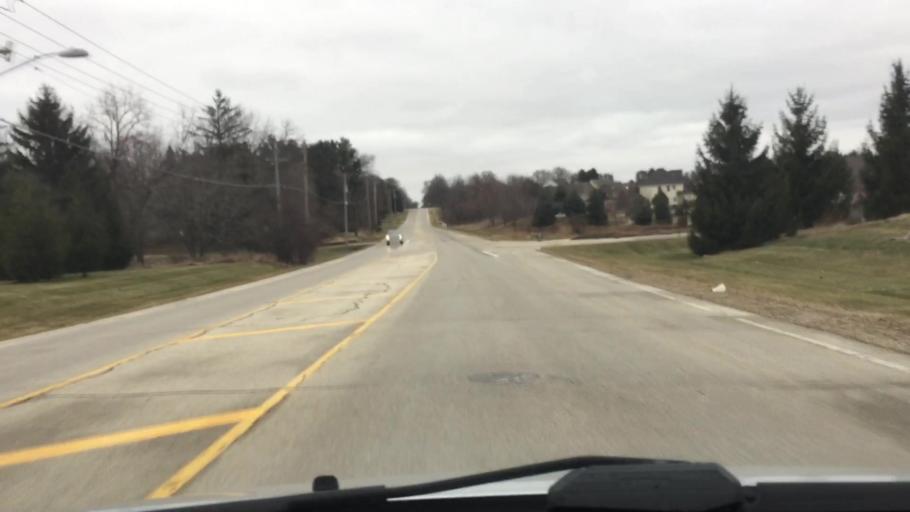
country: US
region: Wisconsin
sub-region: Waukesha County
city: Delafield
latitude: 43.0720
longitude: -88.4037
